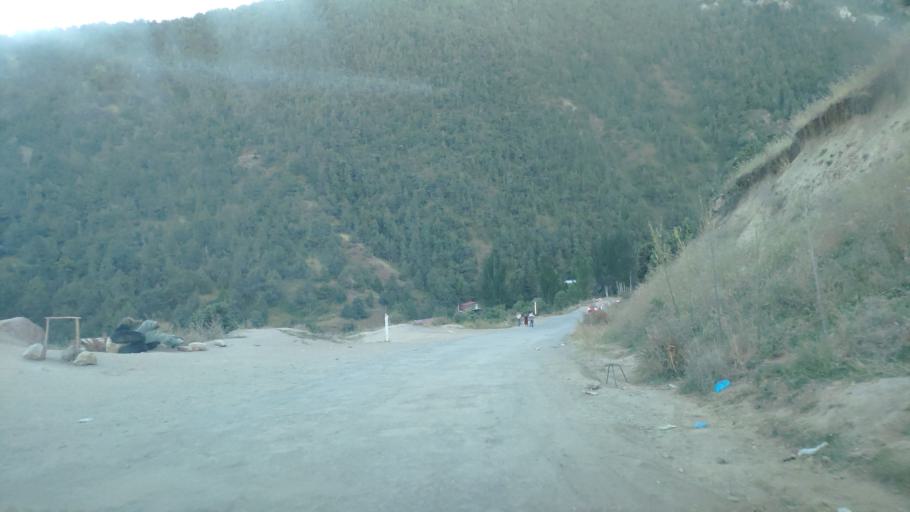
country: TJ
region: Viloyati Sughd
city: Ayni
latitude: 39.6319
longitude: 68.4922
